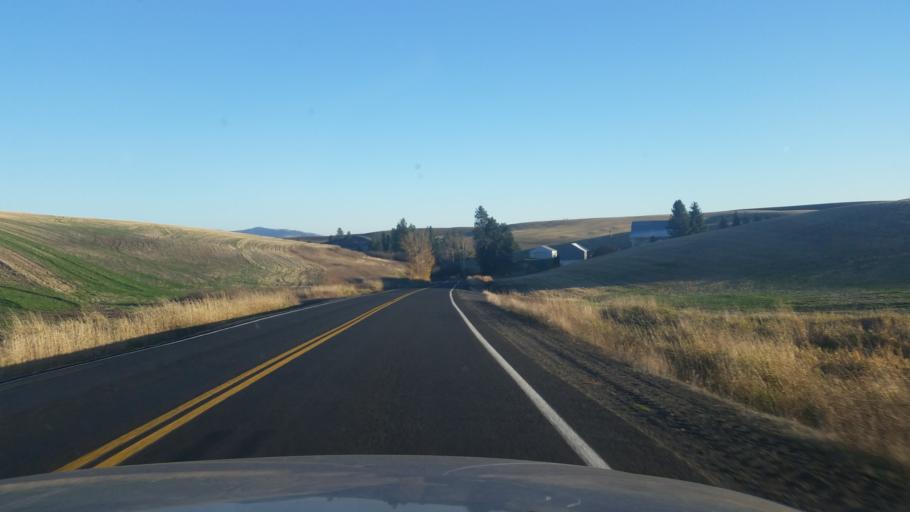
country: US
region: Washington
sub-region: Spokane County
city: Opportunity
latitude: 47.3549
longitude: -117.2653
